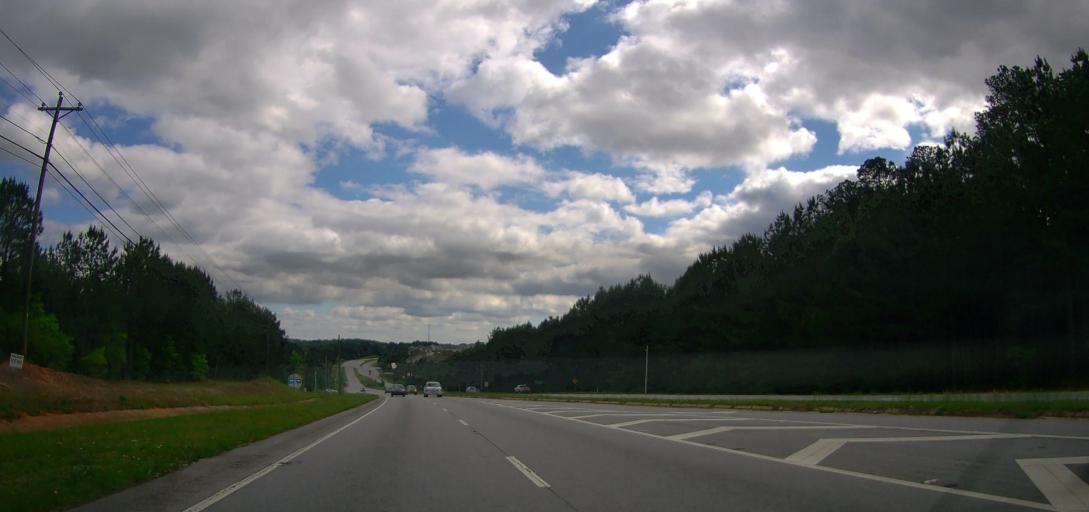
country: US
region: Georgia
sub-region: Rockdale County
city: Conyers
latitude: 33.6913
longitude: -83.9615
